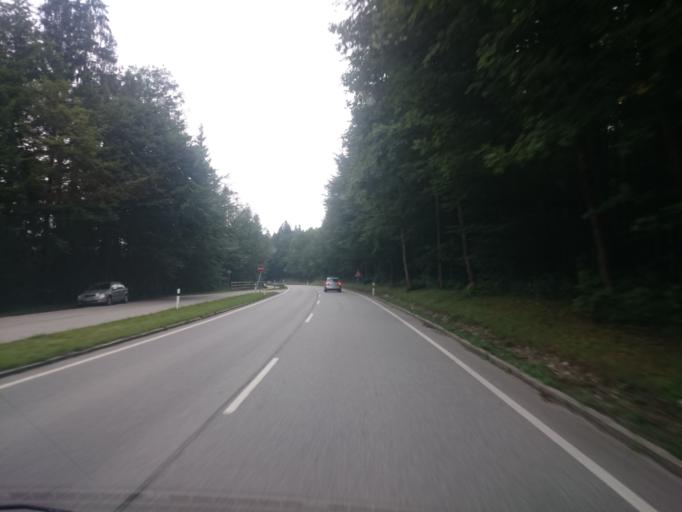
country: DE
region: Bavaria
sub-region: Upper Bavaria
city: Lenggries
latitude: 47.6223
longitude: 11.5955
